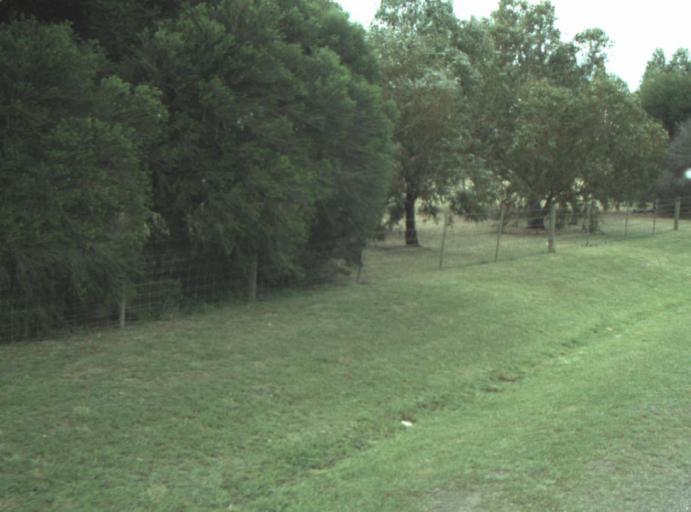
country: AU
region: Victoria
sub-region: Greater Geelong
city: Bell Post Hill
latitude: -38.0594
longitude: 144.3215
